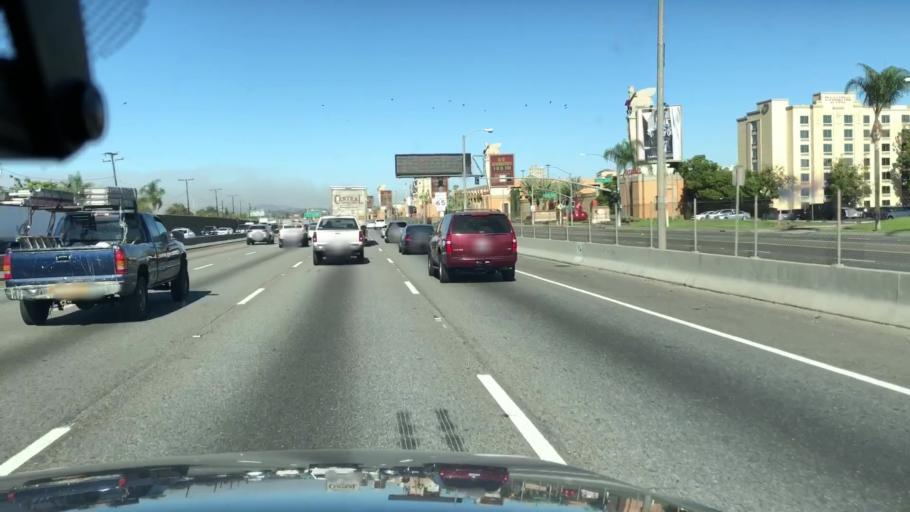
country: US
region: California
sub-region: Los Angeles County
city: Commerce
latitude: 34.0020
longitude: -118.1504
